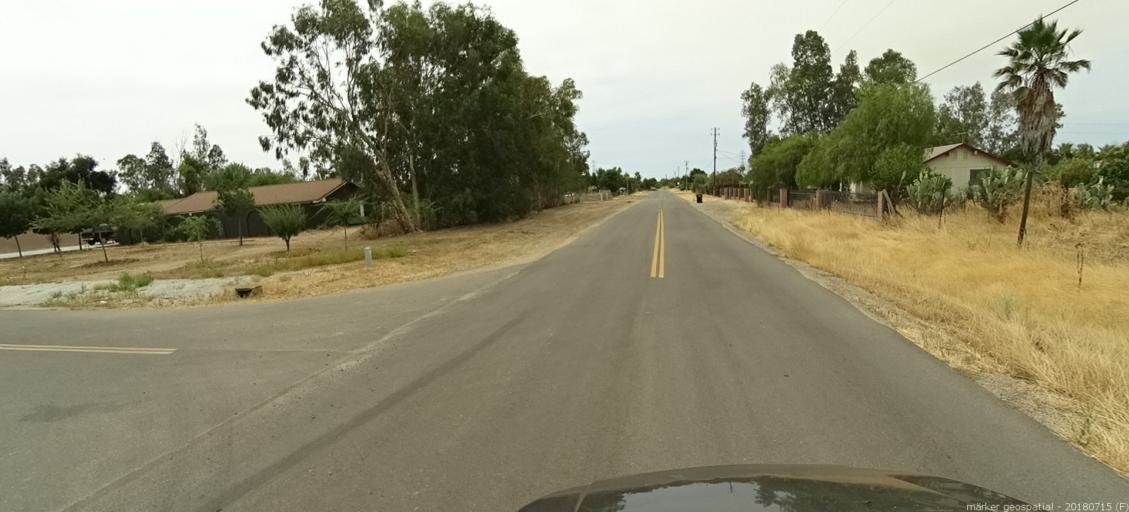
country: US
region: California
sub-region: Madera County
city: Madera Acres
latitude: 37.0234
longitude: -120.0834
